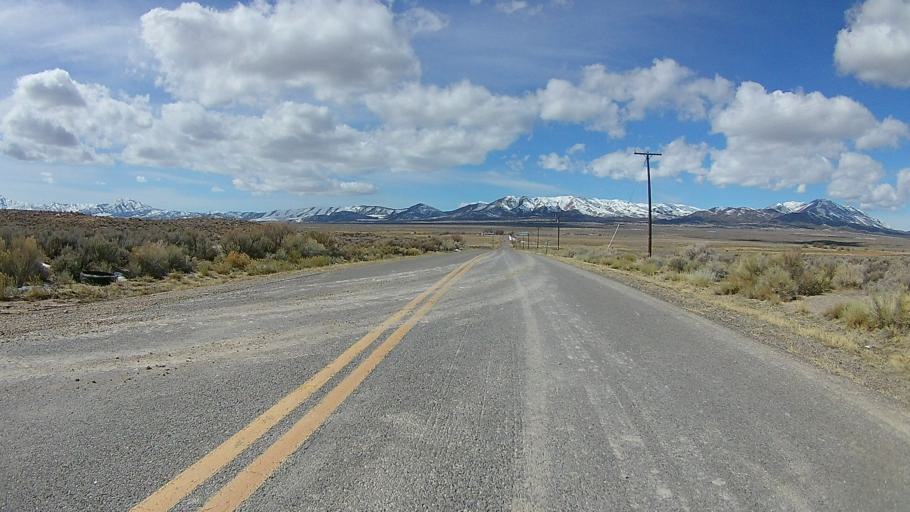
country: US
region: Utah
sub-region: Tooele County
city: Tooele
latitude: 40.1737
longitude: -112.4110
